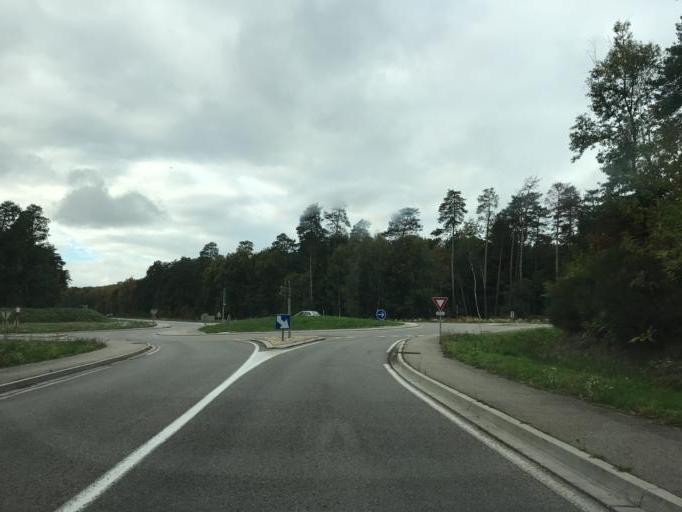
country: FR
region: Rhone-Alpes
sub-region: Departement de l'Ain
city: Bourg-en-Bresse
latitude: 46.2180
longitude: 5.2655
